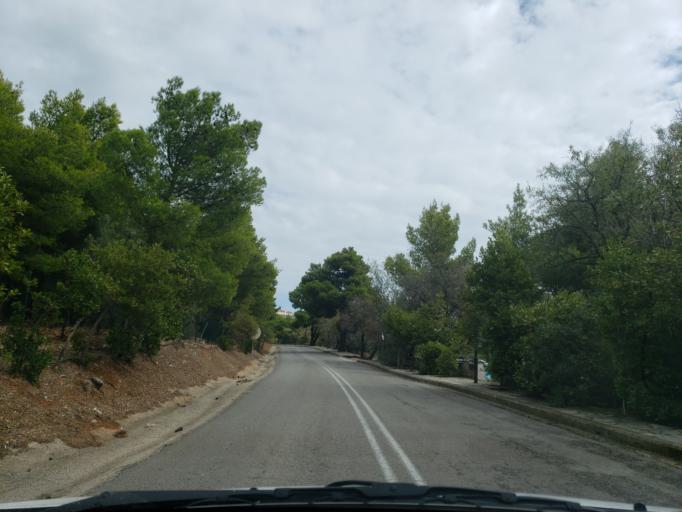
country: GR
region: Central Greece
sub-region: Nomos Fokidos
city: Delphi
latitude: 38.4822
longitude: 22.4850
